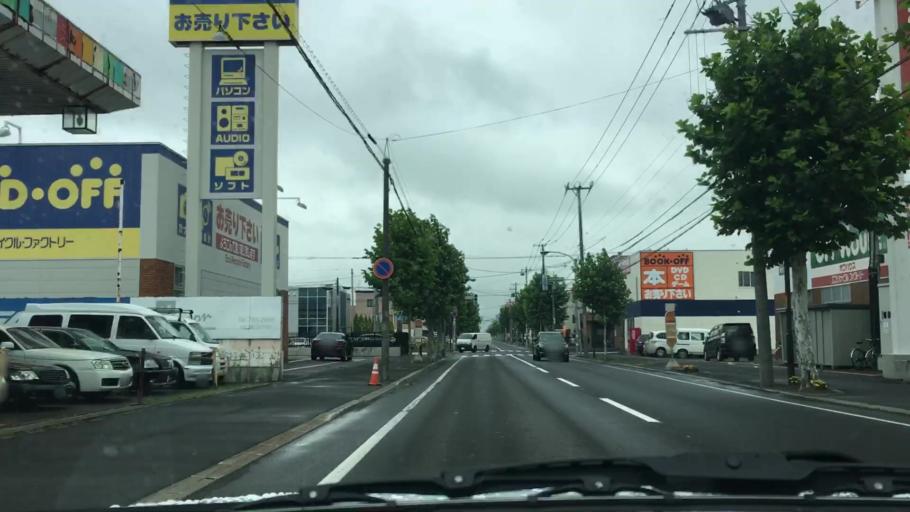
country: JP
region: Hokkaido
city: Sapporo
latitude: 43.0836
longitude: 141.3904
